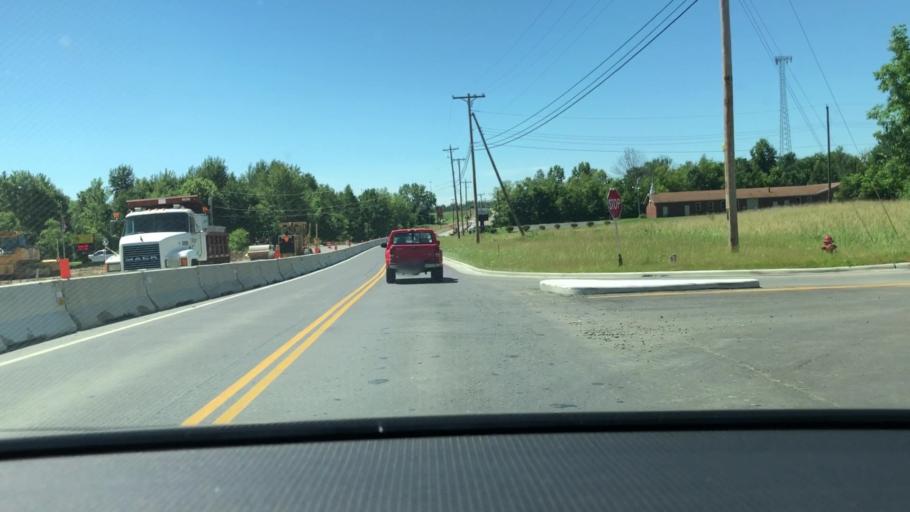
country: US
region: Ohio
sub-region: Licking County
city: Etna
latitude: 39.9565
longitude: -82.6828
